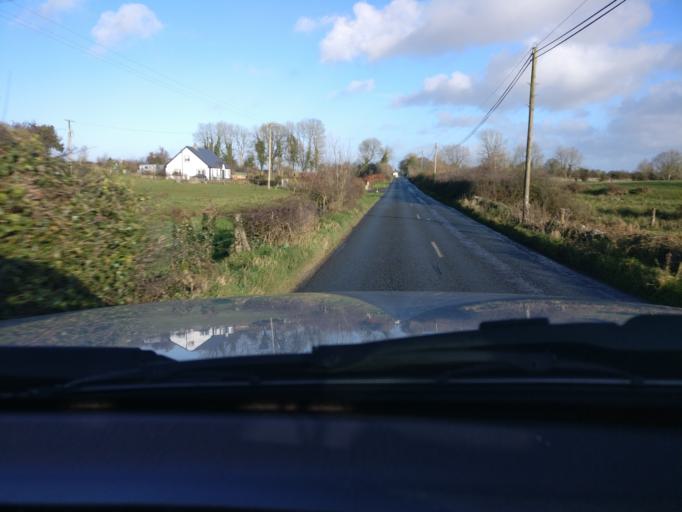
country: IE
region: Leinster
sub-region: An Iarmhi
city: Kilbeggan
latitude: 53.4585
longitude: -7.5114
